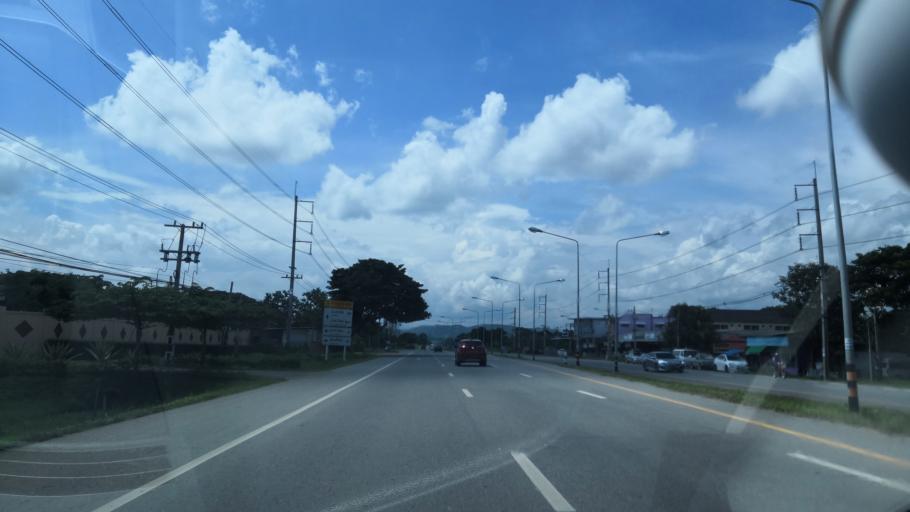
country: TH
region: Chiang Mai
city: Hang Dong
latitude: 18.7217
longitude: 98.9540
